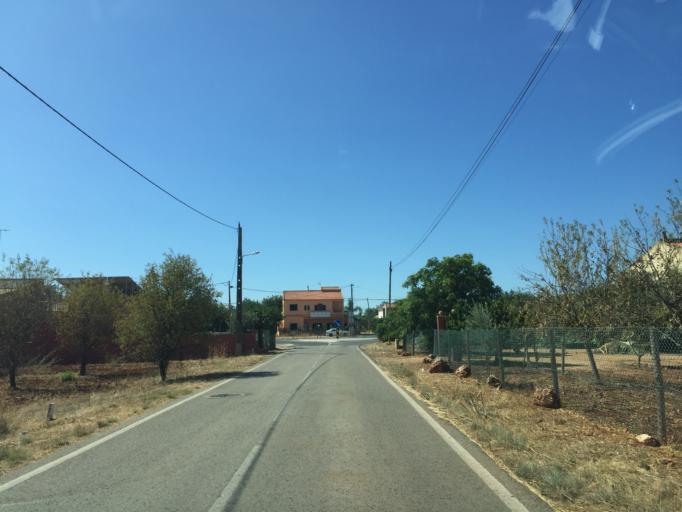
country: PT
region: Faro
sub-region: Loule
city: Vilamoura
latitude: 37.1119
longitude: -8.1005
